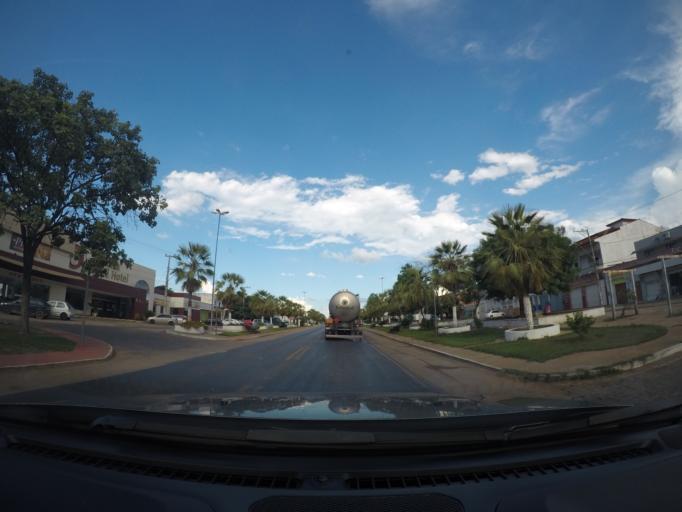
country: BR
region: Bahia
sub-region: Ibotirama
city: Ibotirama
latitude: -12.1785
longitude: -43.2205
